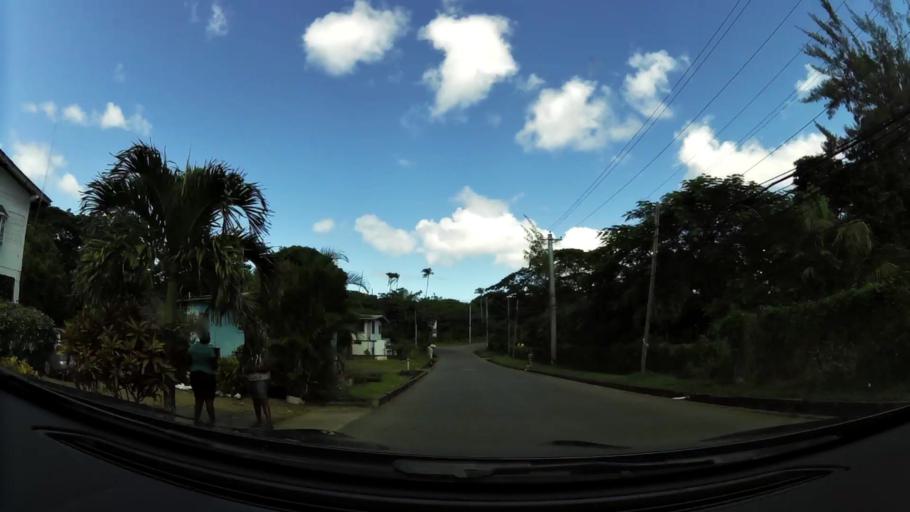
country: TT
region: Tobago
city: Scarborough
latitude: 11.2086
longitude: -60.7796
